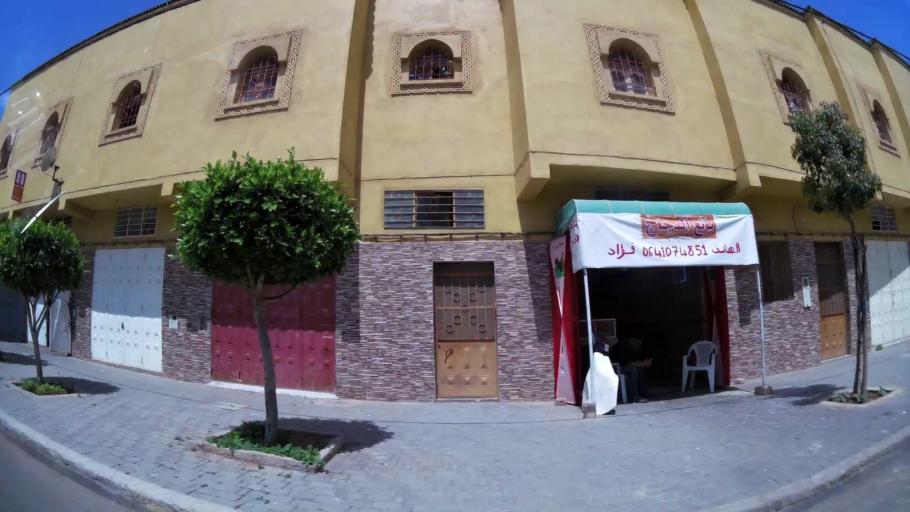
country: MA
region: Oriental
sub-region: Oujda-Angad
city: Oujda
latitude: 34.6851
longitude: -1.8845
